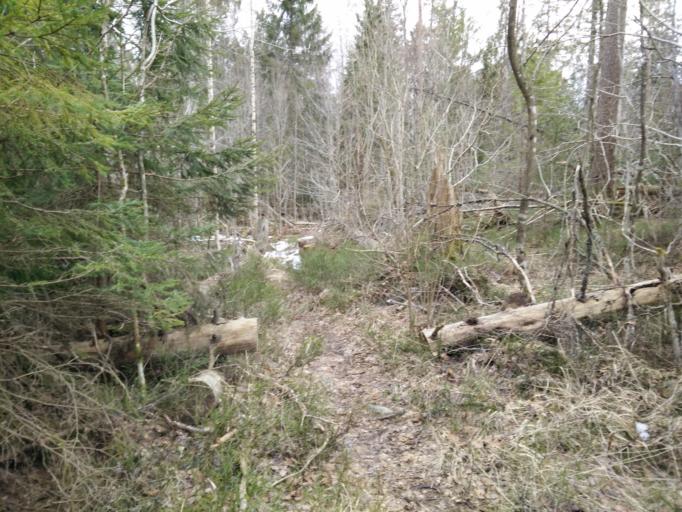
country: SE
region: OErebro
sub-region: Orebro Kommun
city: Garphyttan
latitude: 59.2838
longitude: 14.8894
